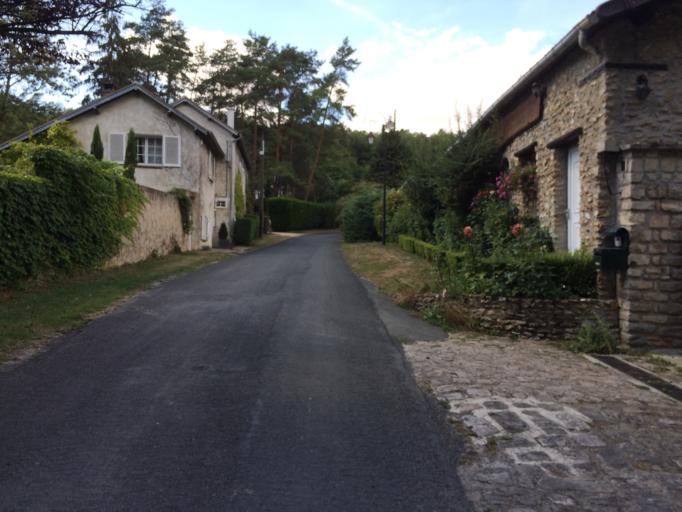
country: FR
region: Centre
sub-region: Departement du Loiret
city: Malesherbes
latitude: 48.3384
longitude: 2.3788
